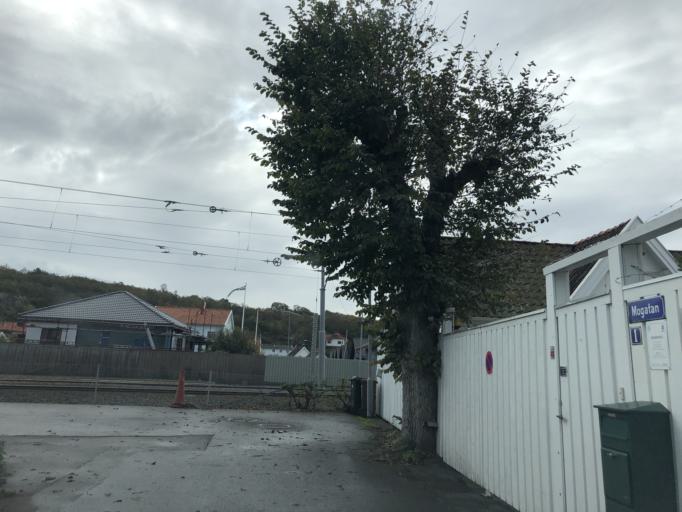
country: SE
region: Vaestra Goetaland
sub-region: Goteborg
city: Majorna
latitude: 57.6676
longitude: 11.8638
